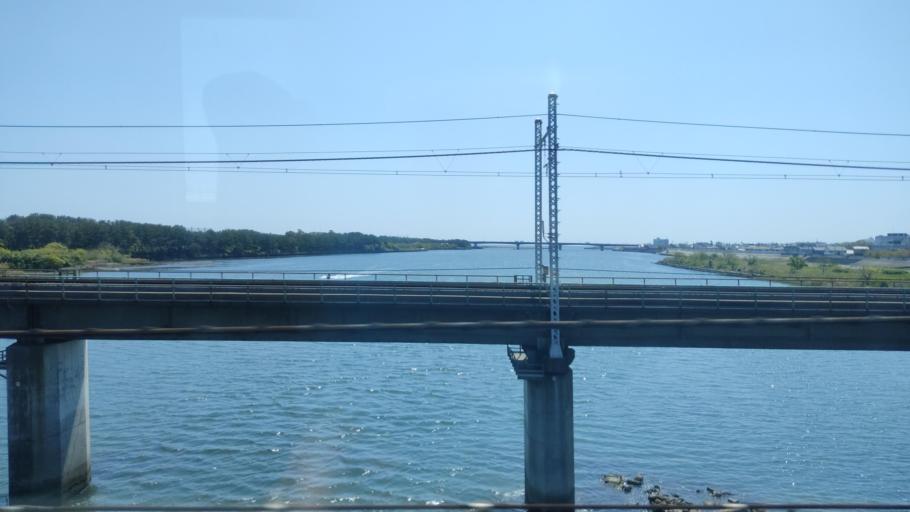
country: JP
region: Kanagawa
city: Hiratsuka
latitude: 35.3309
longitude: 139.3668
